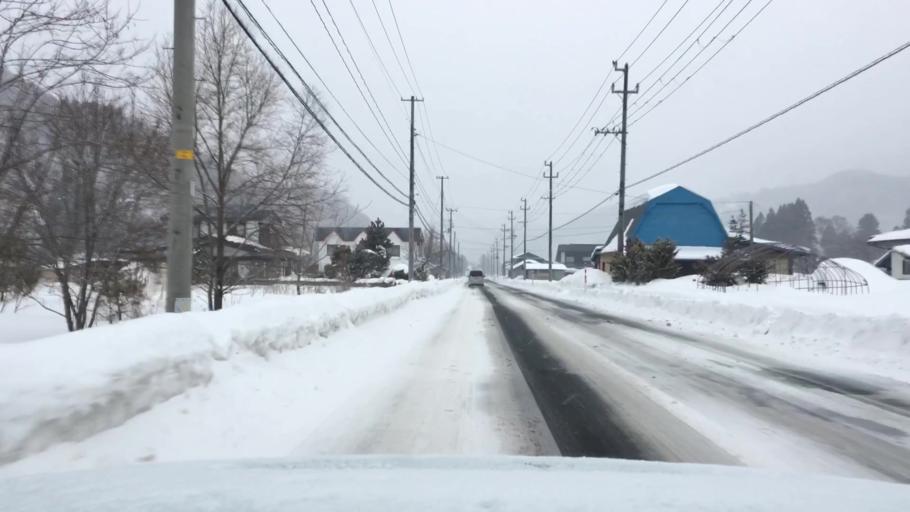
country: JP
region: Akita
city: Hanawa
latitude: 40.0559
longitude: 141.0093
